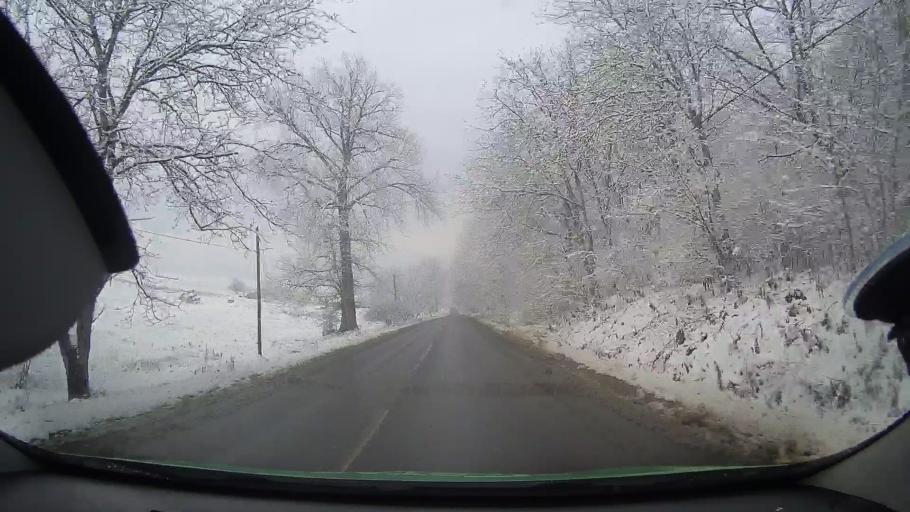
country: RO
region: Mures
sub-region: Comuna Atintis
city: Atintis
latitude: 46.4456
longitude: 24.0897
